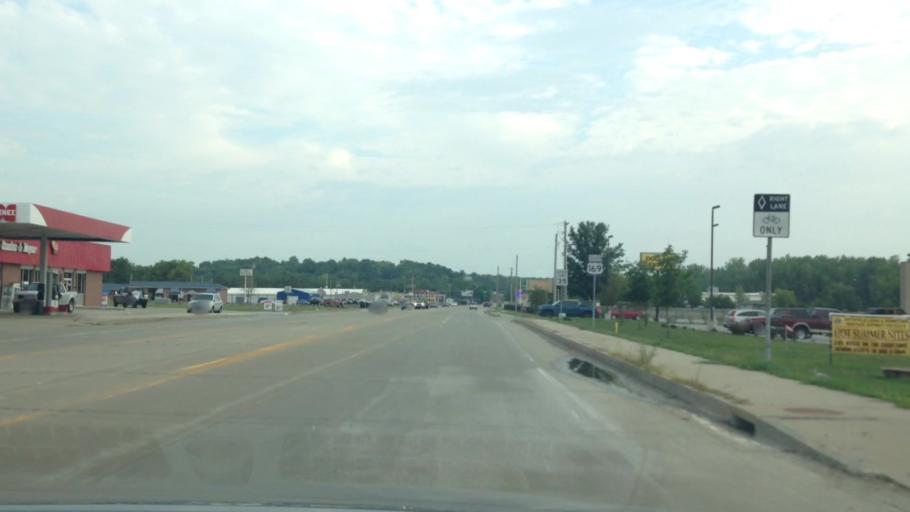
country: US
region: Missouri
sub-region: Clay County
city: Smithville
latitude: 39.3941
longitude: -94.5836
